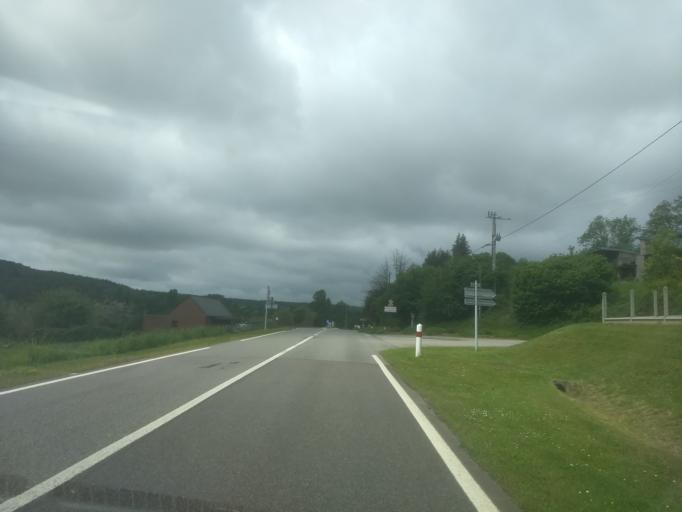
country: FR
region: Lower Normandy
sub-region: Departement de l'Orne
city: Bretoncelles
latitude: 48.4757
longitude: 0.8572
